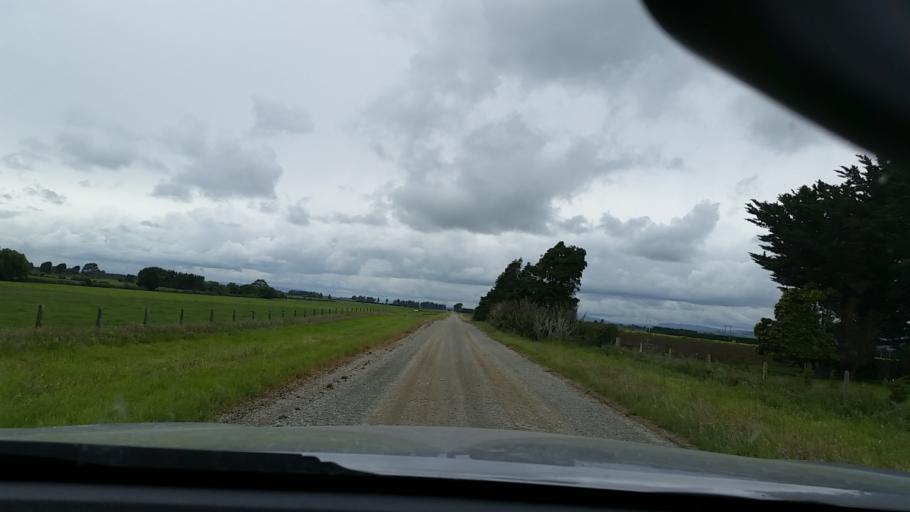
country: NZ
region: Southland
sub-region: Southland District
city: Winton
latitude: -46.2660
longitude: 168.3674
